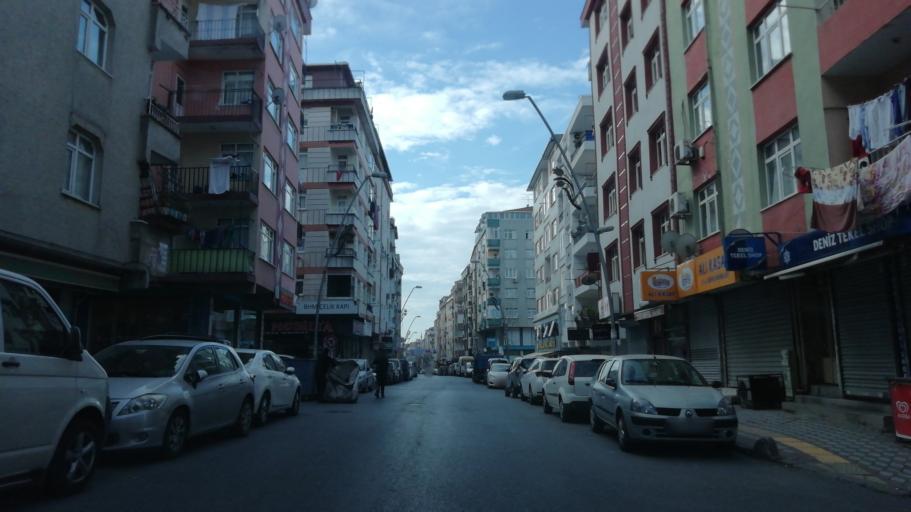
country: TR
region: Istanbul
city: Bahcelievler
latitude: 40.9983
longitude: 28.8407
